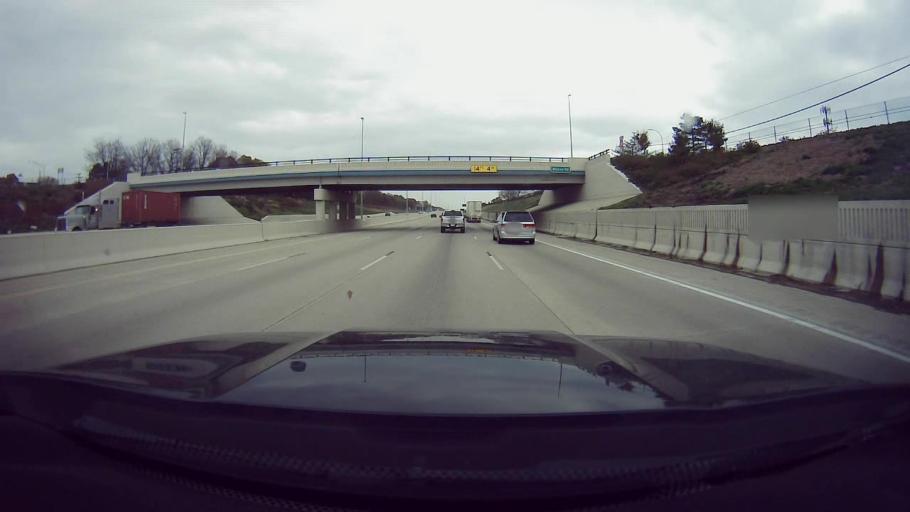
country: US
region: Michigan
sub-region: Wayne County
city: Livonia
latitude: 42.3821
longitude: -83.3891
